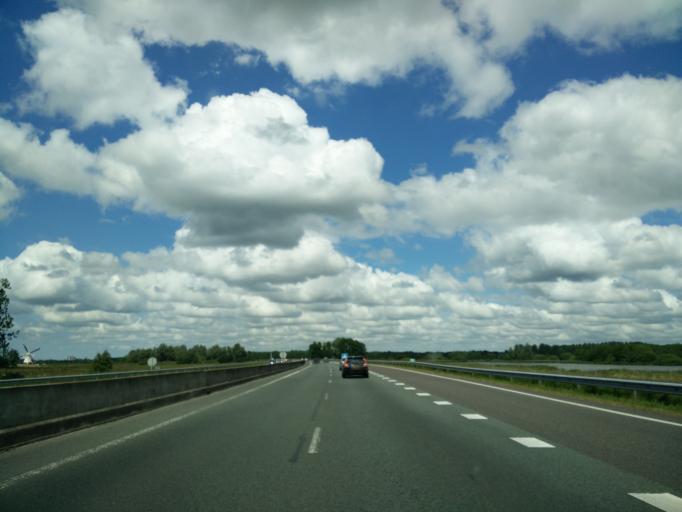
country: NL
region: Groningen
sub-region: Gemeente Haren
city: Haren
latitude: 53.1413
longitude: 6.6081
